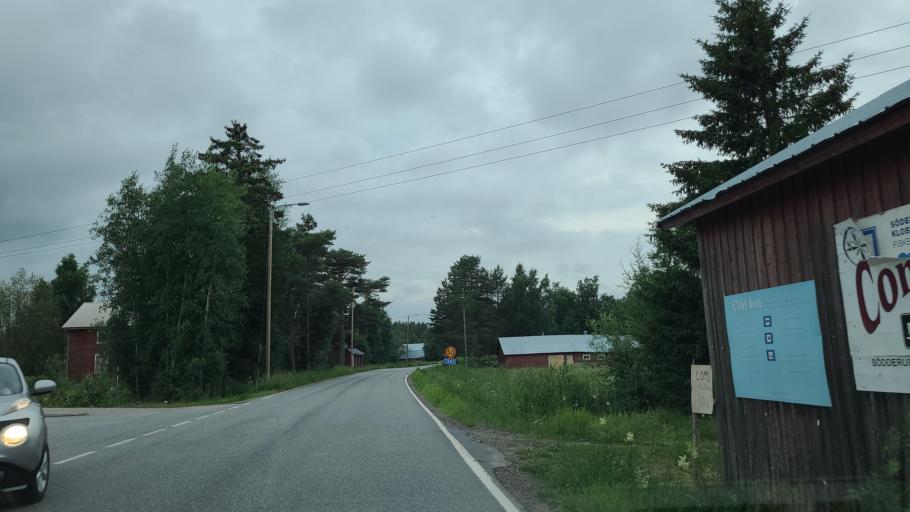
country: FI
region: Ostrobothnia
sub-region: Vaasa
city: Replot
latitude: 63.2322
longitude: 21.4073
